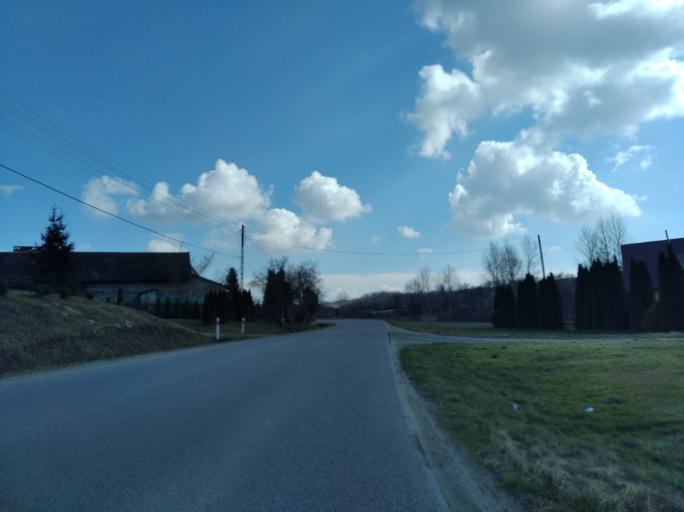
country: PL
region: Subcarpathian Voivodeship
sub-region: Powiat debicki
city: Brzostek
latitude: 49.8612
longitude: 21.4686
